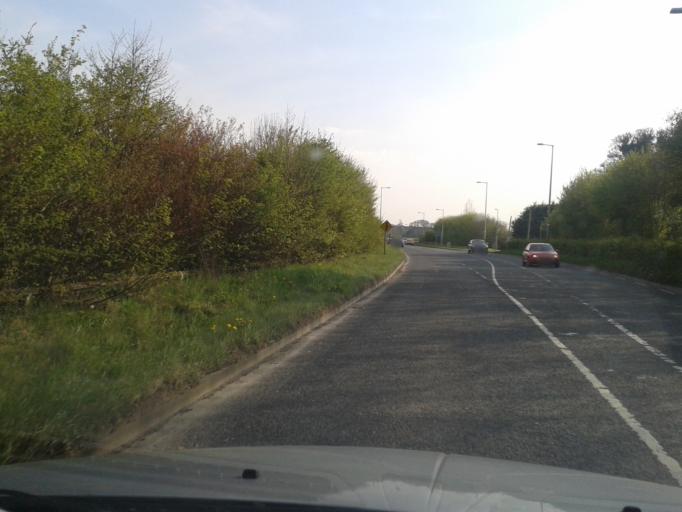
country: IE
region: Leinster
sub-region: Dublin City
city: Finglas
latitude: 53.4266
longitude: -6.3045
